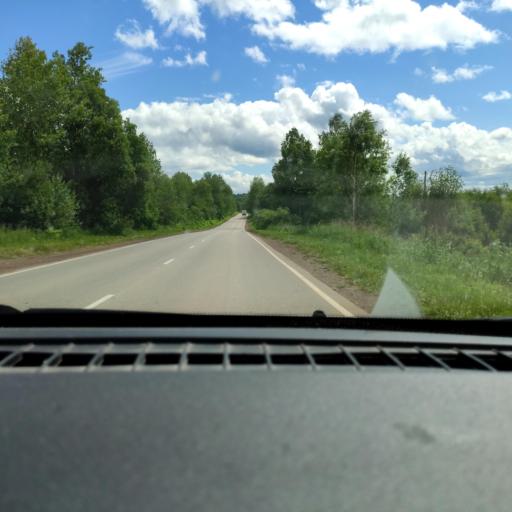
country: RU
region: Perm
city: Overyata
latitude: 58.1199
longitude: 55.8218
